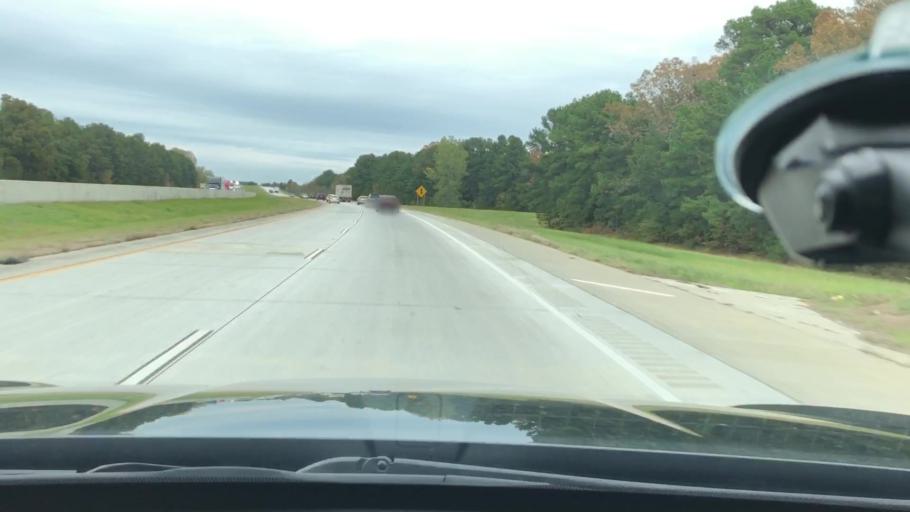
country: US
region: Arkansas
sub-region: Hempstead County
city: Hope
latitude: 33.6107
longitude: -93.7992
